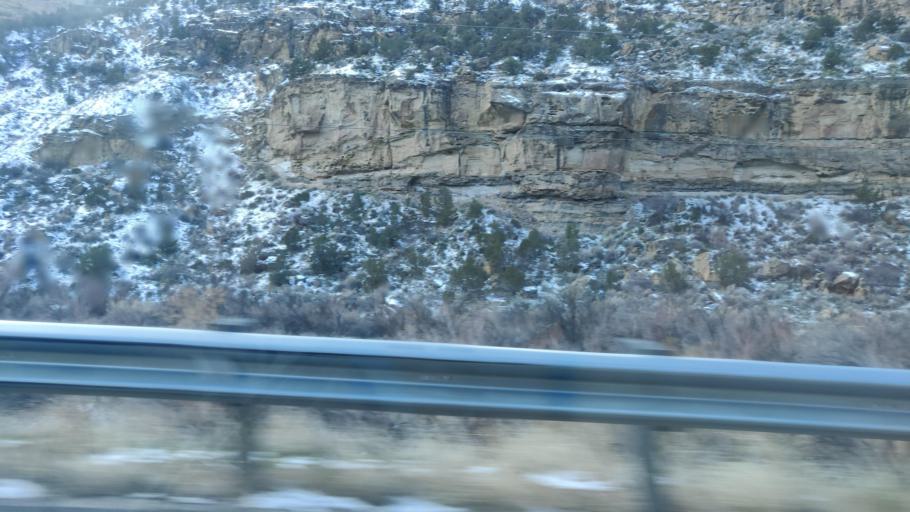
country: US
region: Colorado
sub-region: Mesa County
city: Palisade
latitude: 39.1886
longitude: -108.2471
